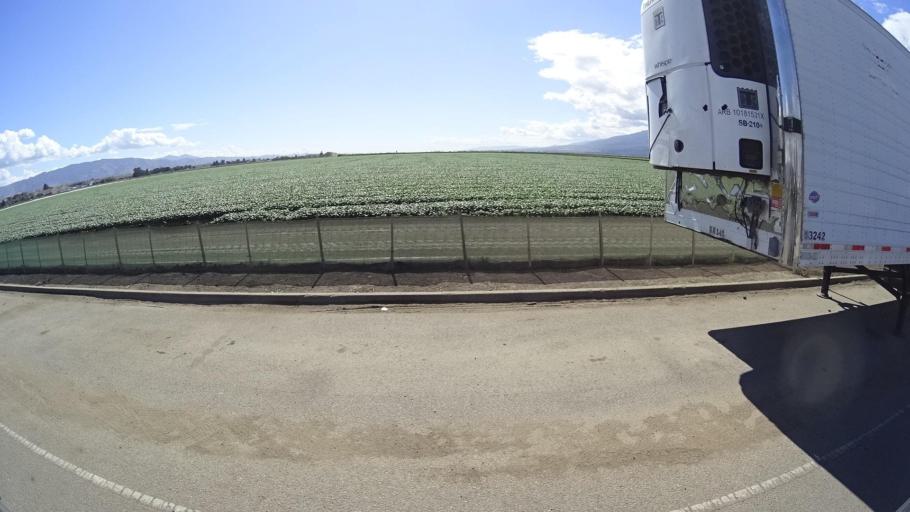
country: US
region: California
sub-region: Monterey County
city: Gonzales
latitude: 36.5007
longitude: -121.4478
